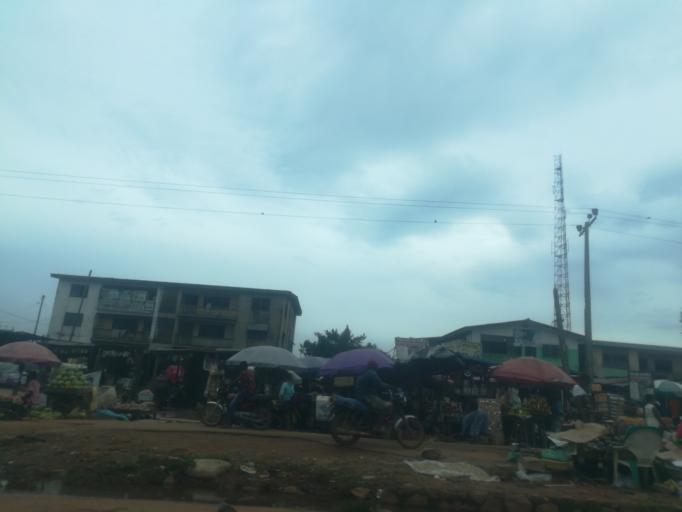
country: NG
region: Oyo
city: Egbeda
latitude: 7.3850
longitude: 3.9869
